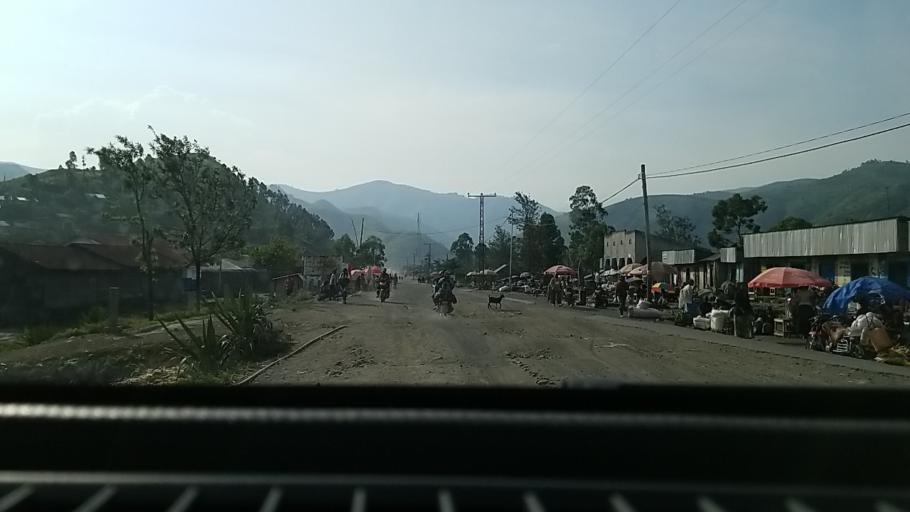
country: CD
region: Nord Kivu
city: Sake
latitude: -1.5726
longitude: 29.0597
